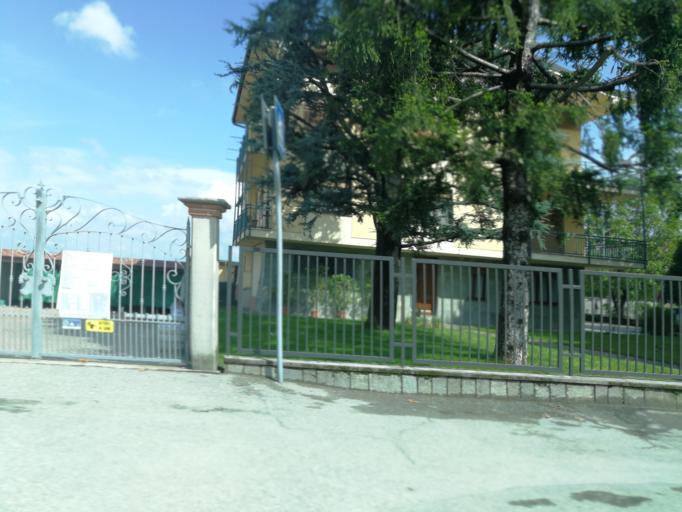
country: IT
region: Piedmont
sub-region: Provincia di Cuneo
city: Moretta
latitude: 44.7666
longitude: 7.5440
